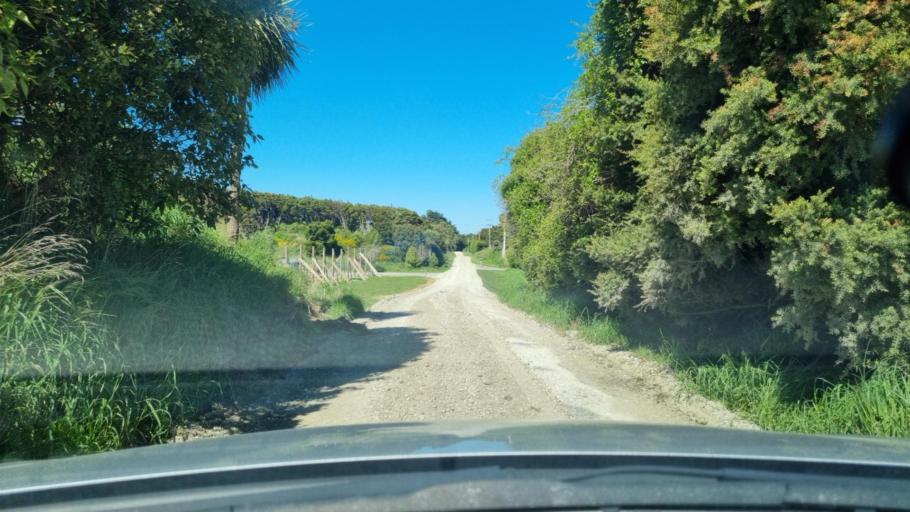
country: NZ
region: Southland
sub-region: Invercargill City
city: Invercargill
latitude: -46.4536
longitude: 168.2813
